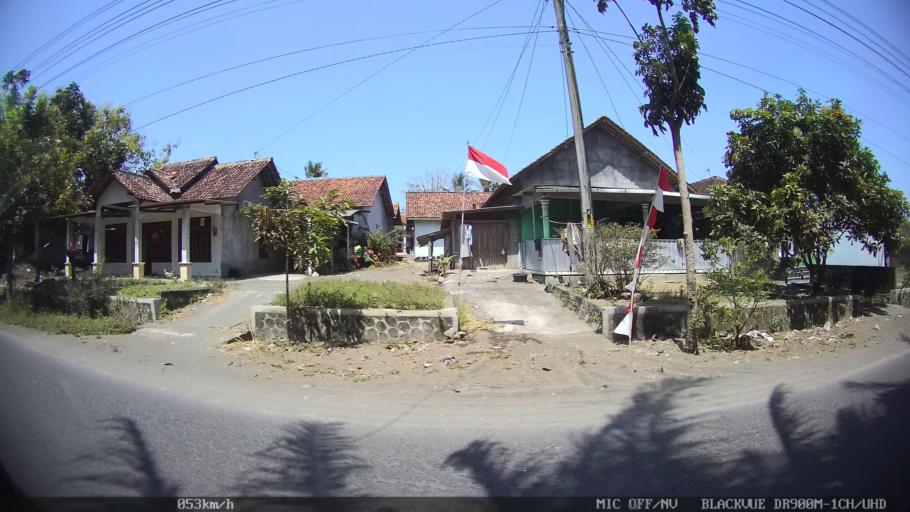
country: ID
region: Daerah Istimewa Yogyakarta
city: Srandakan
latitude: -7.9201
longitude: 110.1111
